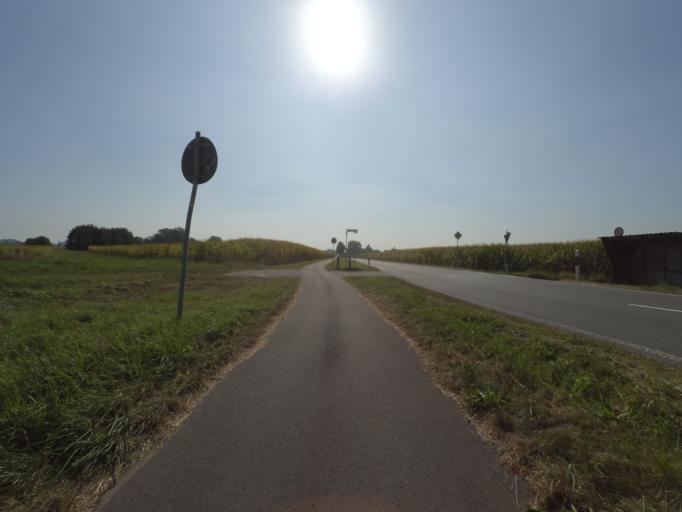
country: DE
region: North Rhine-Westphalia
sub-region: Regierungsbezirk Munster
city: Schoppingen
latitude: 52.0795
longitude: 7.2321
